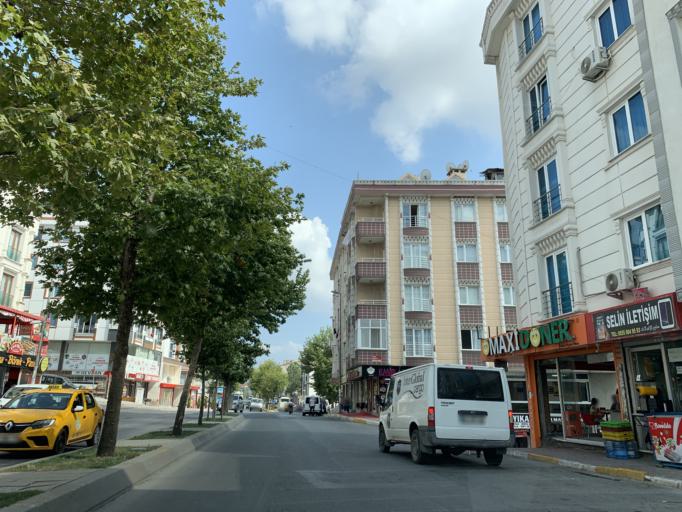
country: TR
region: Istanbul
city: Esenyurt
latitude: 41.0401
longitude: 28.6615
